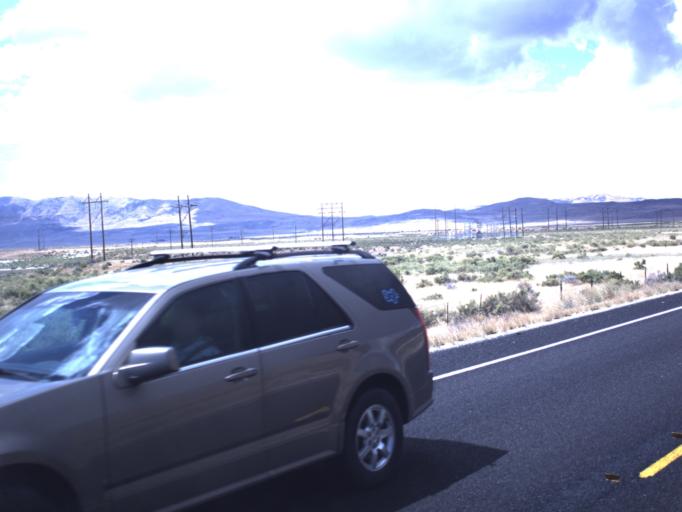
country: US
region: Utah
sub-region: Box Elder County
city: Tremonton
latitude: 41.6183
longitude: -112.3830
